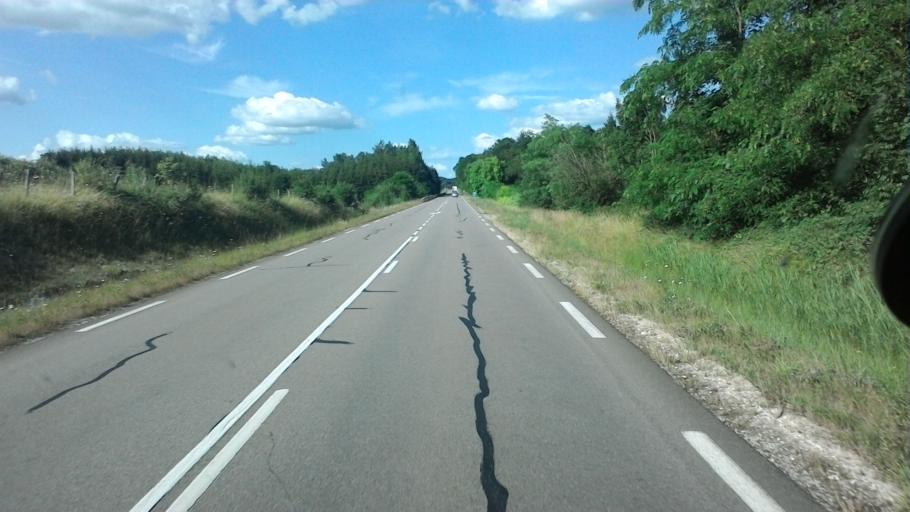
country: FR
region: Franche-Comte
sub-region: Departement de la Haute-Saone
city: Rioz
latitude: 47.5197
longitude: 6.0050
